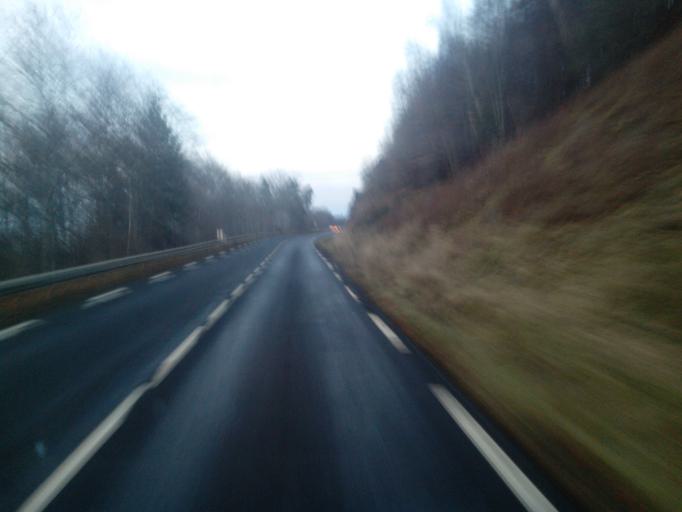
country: FR
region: Auvergne
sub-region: Departement du Cantal
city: Murat
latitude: 45.1026
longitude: 2.9069
